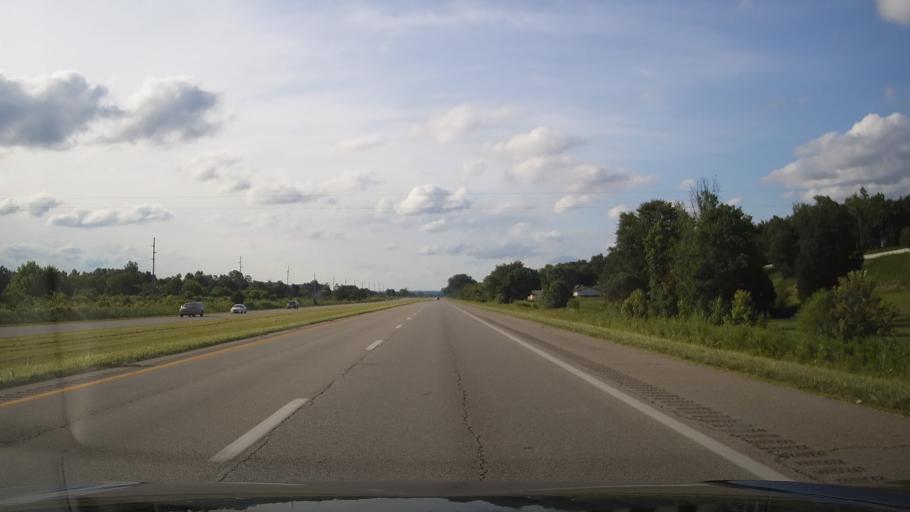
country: US
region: Ohio
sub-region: Scioto County
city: Franklin Furnace
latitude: 38.6651
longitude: -82.8551
